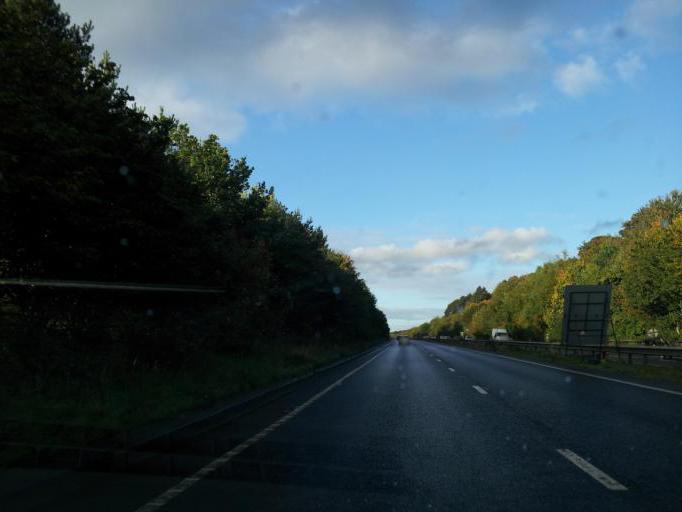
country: GB
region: England
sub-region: Norfolk
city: Thorpe Hamlet
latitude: 52.6201
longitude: 1.3576
